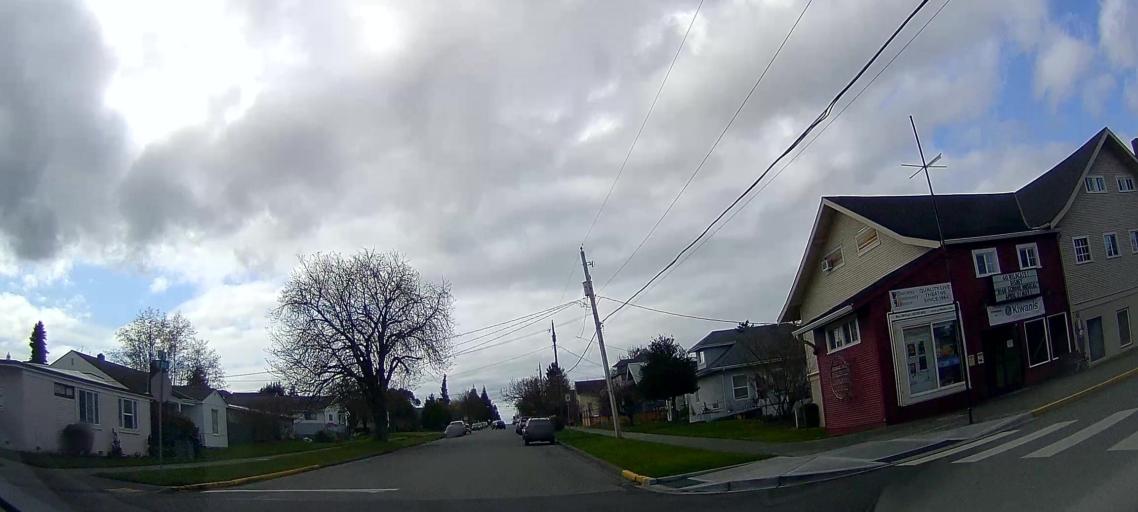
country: US
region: Washington
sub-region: Skagit County
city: Anacortes
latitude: 48.5143
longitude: -122.6173
